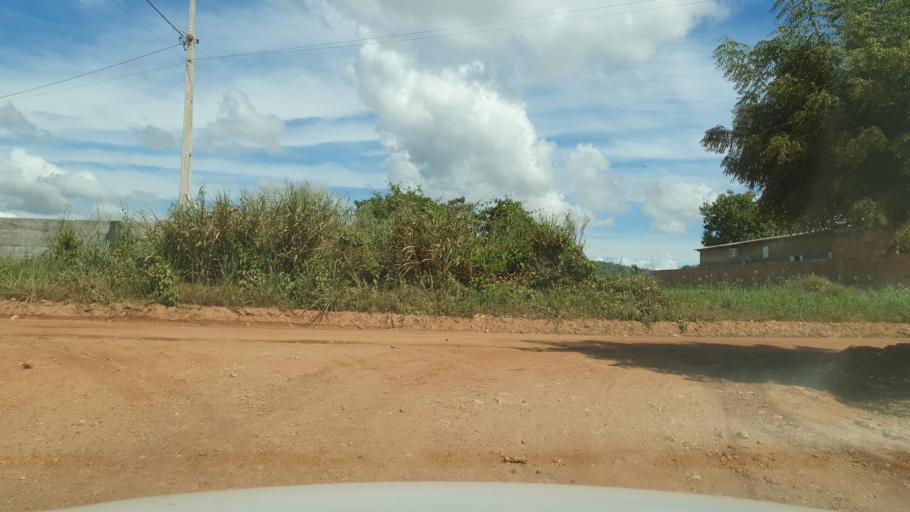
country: BR
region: Mato Grosso
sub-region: Pontes E Lacerda
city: Pontes e Lacerda
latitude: -15.2531
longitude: -59.3153
